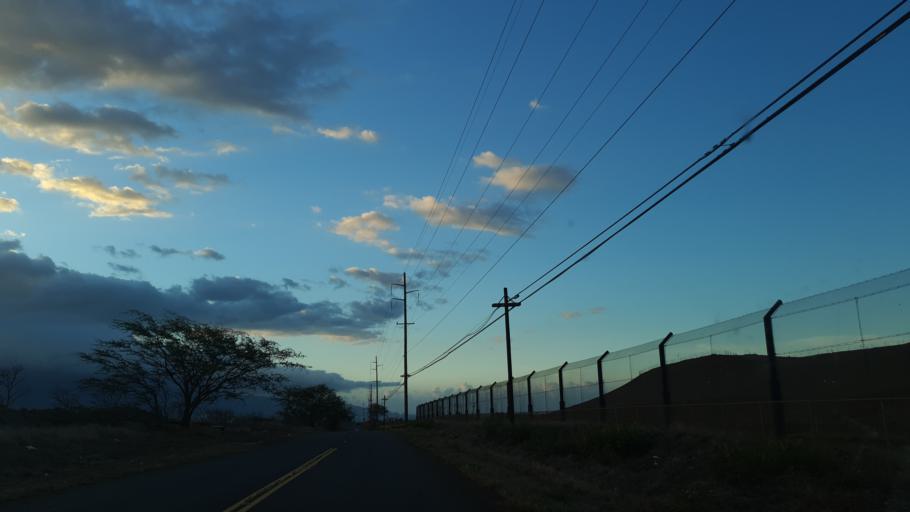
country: US
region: Hawaii
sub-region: Maui County
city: Kahului
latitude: 20.8551
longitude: -156.4217
